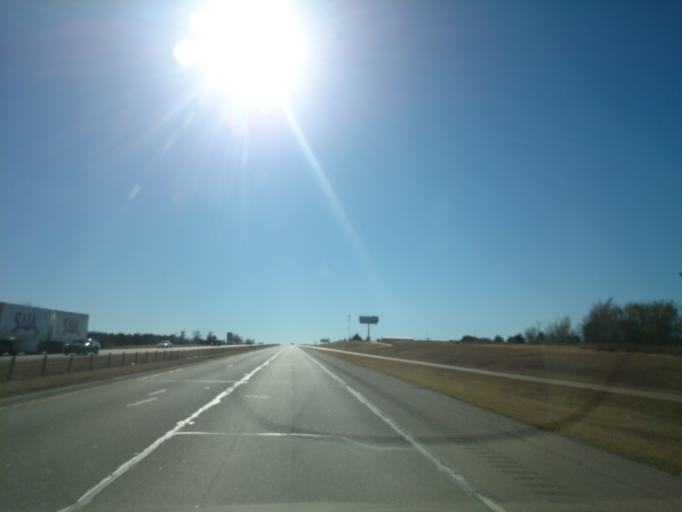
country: US
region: Oklahoma
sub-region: Logan County
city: Guthrie
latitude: 35.8752
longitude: -97.3943
